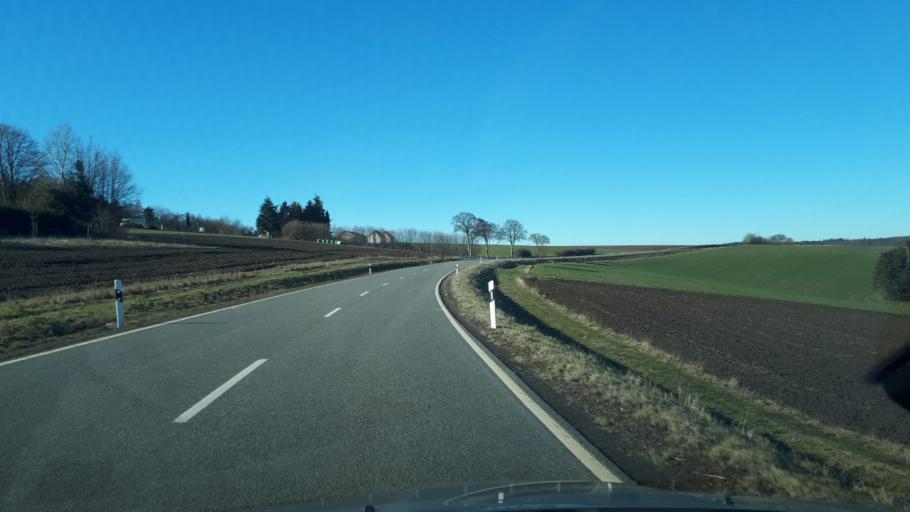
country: DE
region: Rheinland-Pfalz
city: Immerath
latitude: 50.1338
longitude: 6.9344
